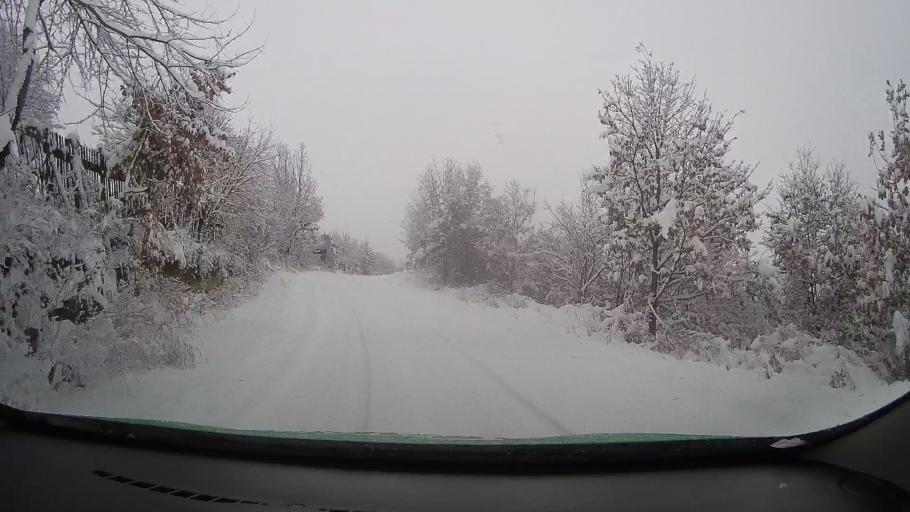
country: RO
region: Hunedoara
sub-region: Comuna Teliucu Inferior
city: Teliucu Inferior
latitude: 45.6976
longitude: 22.8913
